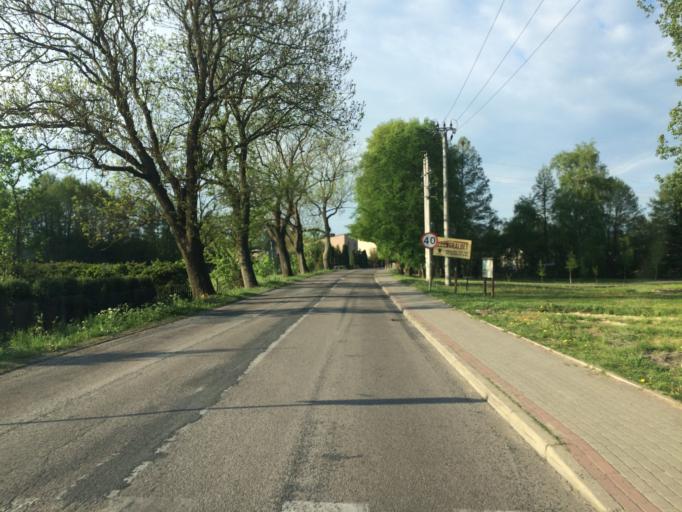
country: PL
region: Warmian-Masurian Voivodeship
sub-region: Powiat dzialdowski
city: Rybno
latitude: 53.3794
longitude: 19.9377
